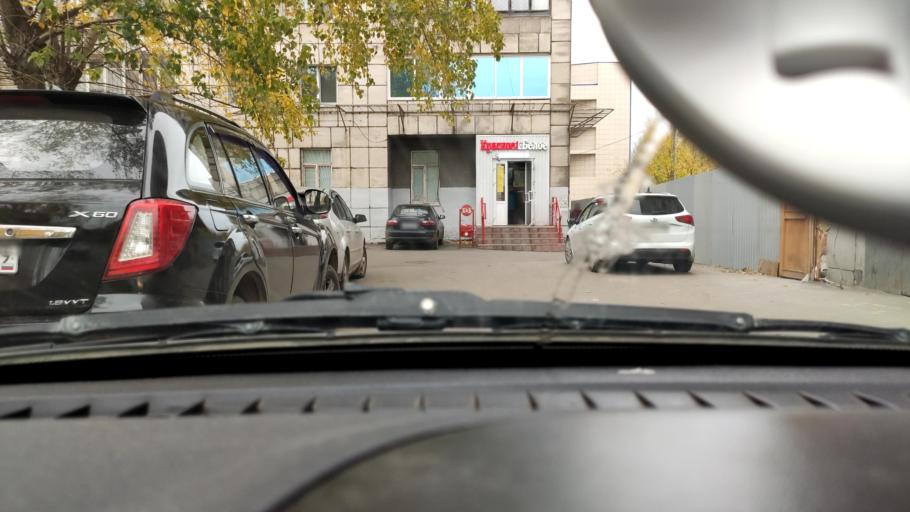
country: RU
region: Perm
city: Perm
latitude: 58.0252
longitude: 56.3040
